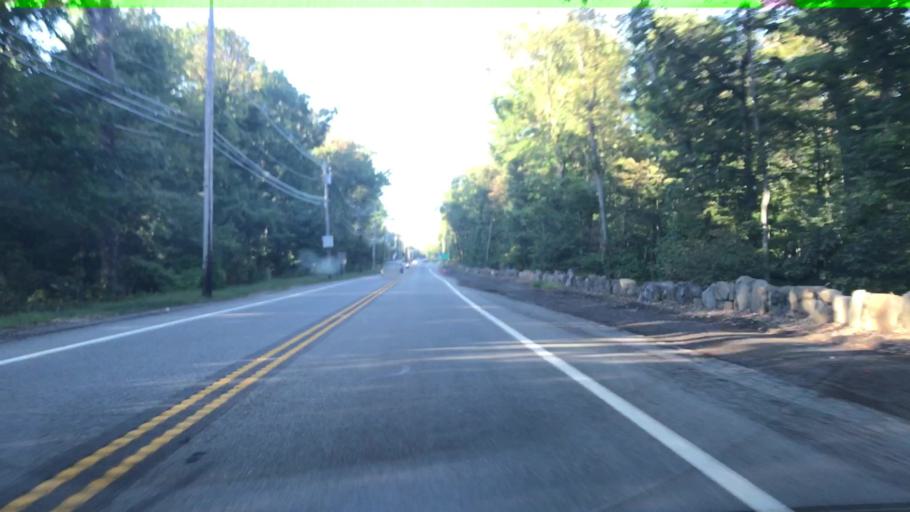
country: US
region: New Jersey
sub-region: Bergen County
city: Alpine
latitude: 40.9277
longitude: -73.9297
